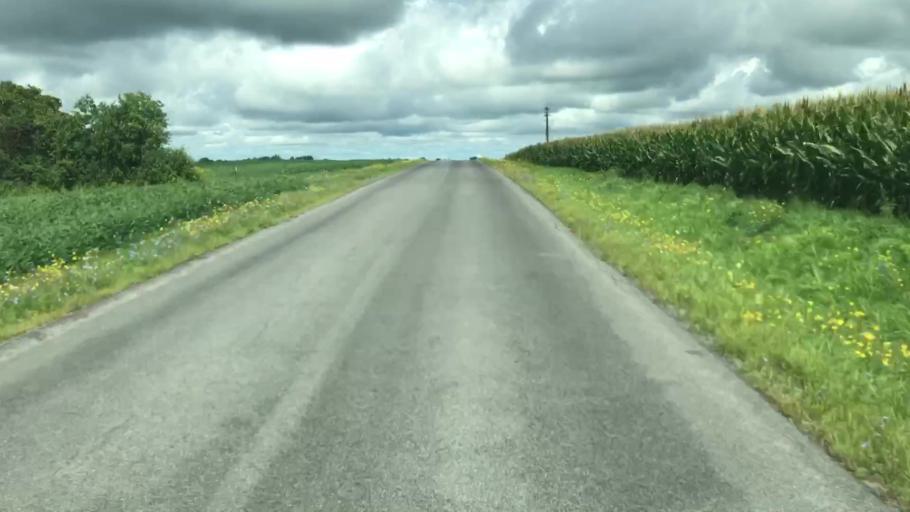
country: US
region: New York
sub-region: Onondaga County
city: Skaneateles
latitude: 42.9373
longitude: -76.4709
